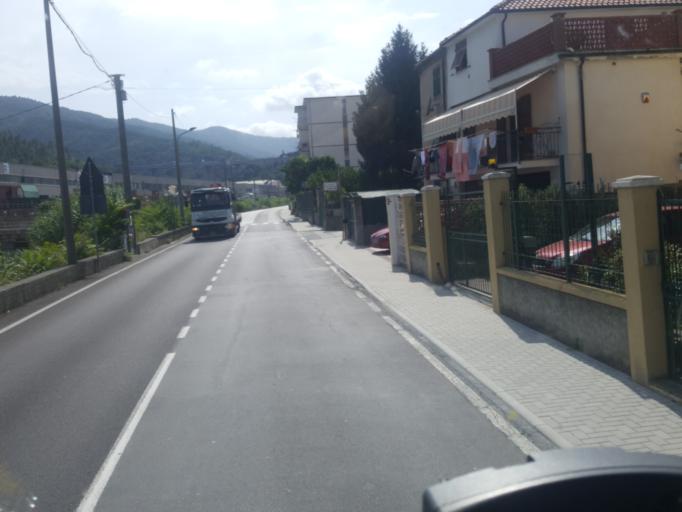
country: IT
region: Liguria
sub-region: Provincia di Savona
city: Valle di Vado
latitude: 44.2617
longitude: 8.4149
